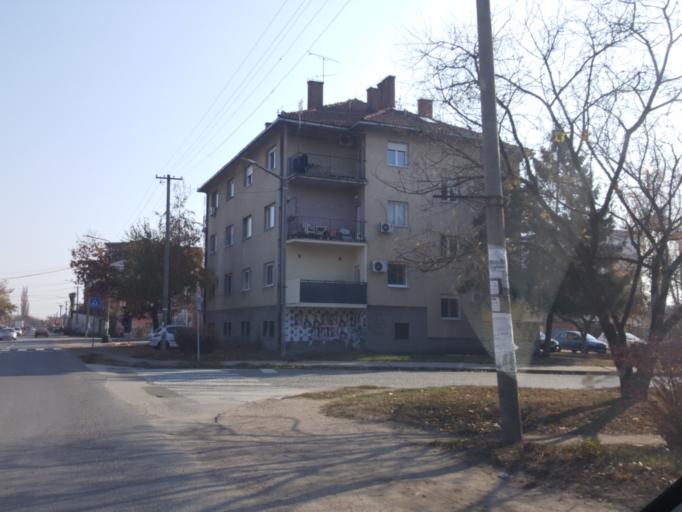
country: RS
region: Central Serbia
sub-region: Borski Okrug
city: Negotin
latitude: 44.2294
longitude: 22.5381
